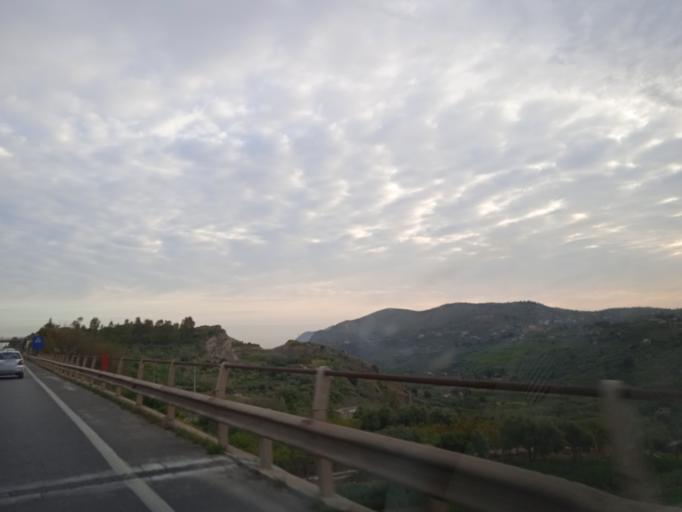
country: IT
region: Sicily
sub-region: Palermo
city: Portella di Mare
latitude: 38.0511
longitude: 13.4615
